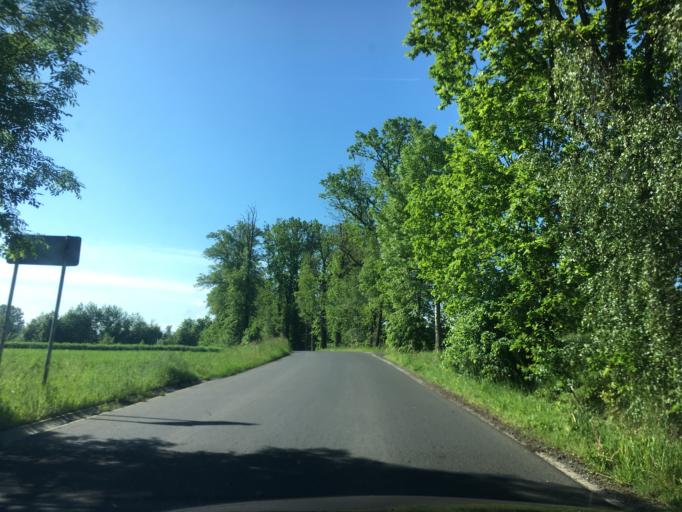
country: PL
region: Lower Silesian Voivodeship
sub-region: Powiat zgorzelecki
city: Zgorzelec
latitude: 51.1093
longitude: 15.0335
